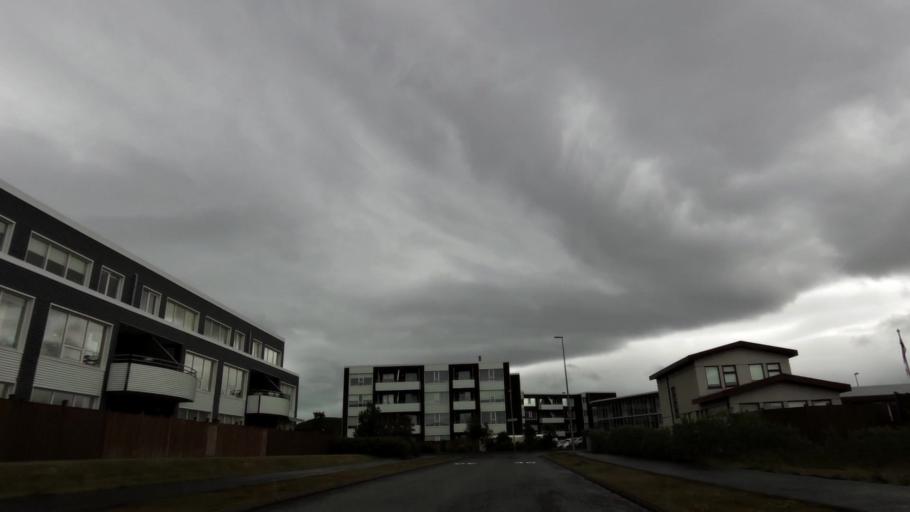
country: IS
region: Capital Region
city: Hafnarfjoerdur
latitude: 64.0495
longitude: -21.9767
